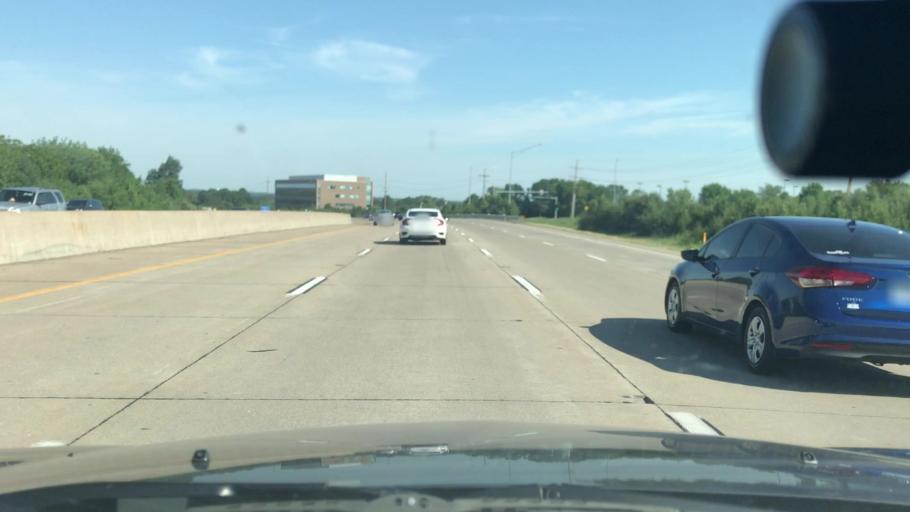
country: US
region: Missouri
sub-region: Saint Charles County
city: Weldon Spring
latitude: 38.7073
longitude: -90.6759
